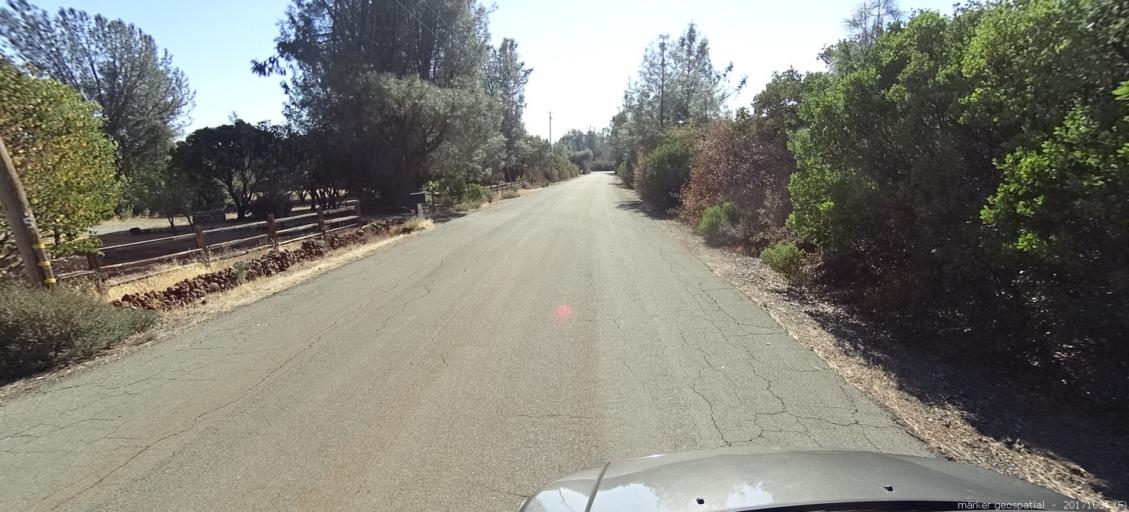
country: US
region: California
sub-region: Shasta County
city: Shingletown
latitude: 40.5109
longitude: -122.0244
